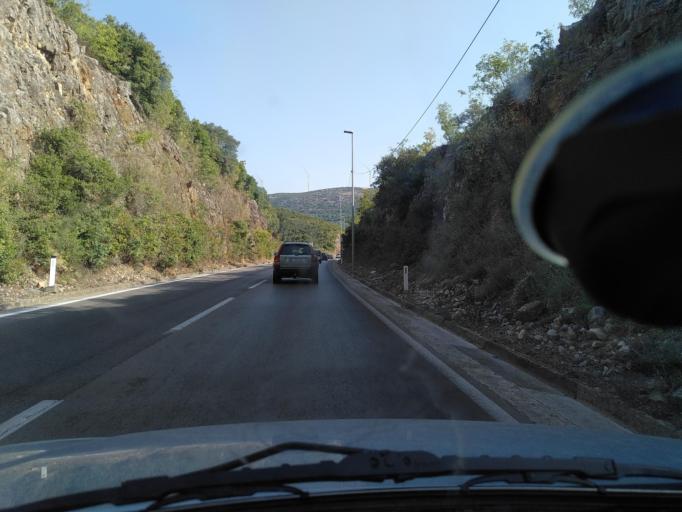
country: ME
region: Ulcinj
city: Ulcinj
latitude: 41.9574
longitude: 19.1908
